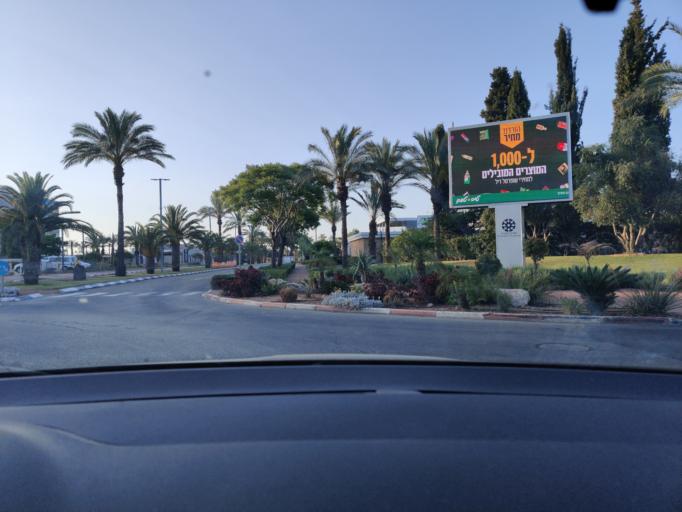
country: IL
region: Haifa
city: Qesarya
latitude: 32.4840
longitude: 34.9483
